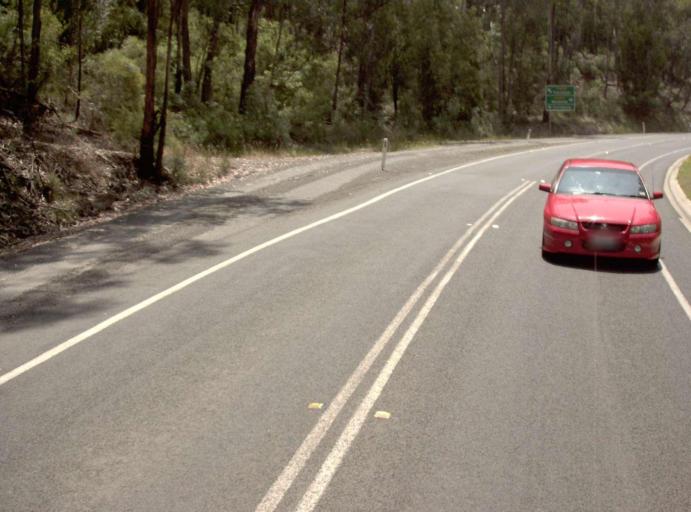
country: AU
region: Victoria
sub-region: Latrobe
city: Traralgon
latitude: -38.3837
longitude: 146.7568
